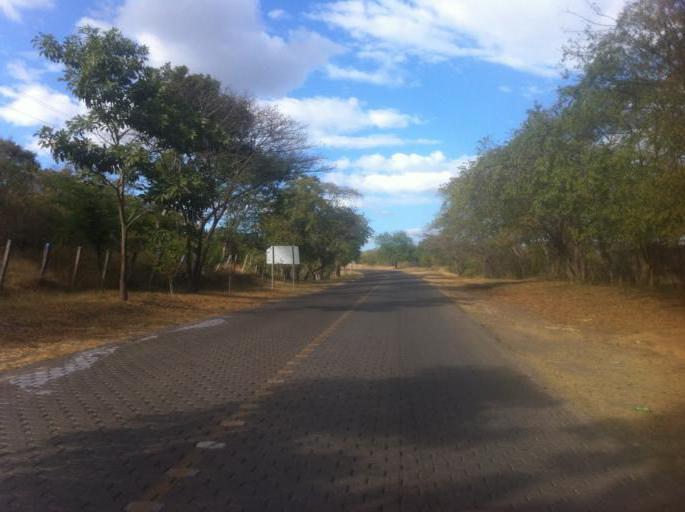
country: NI
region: Managua
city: Masachapa
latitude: 11.8275
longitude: -86.5030
